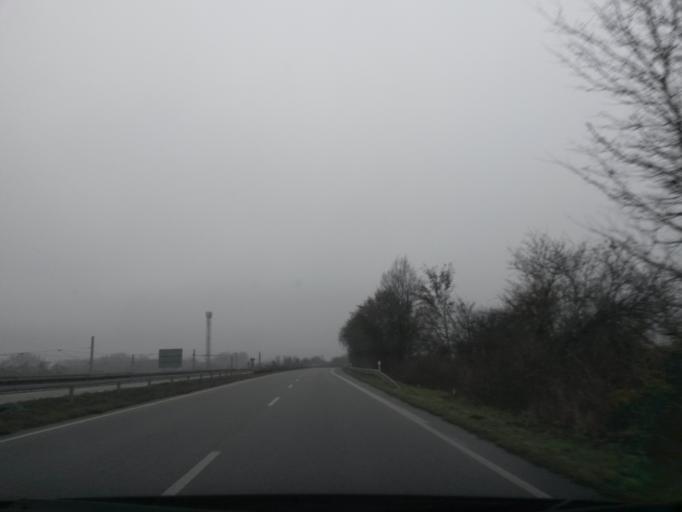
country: DE
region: Baden-Wuerttemberg
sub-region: Karlsruhe Region
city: Eggenstein-Leopoldshafen
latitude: 49.0589
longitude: 8.3926
